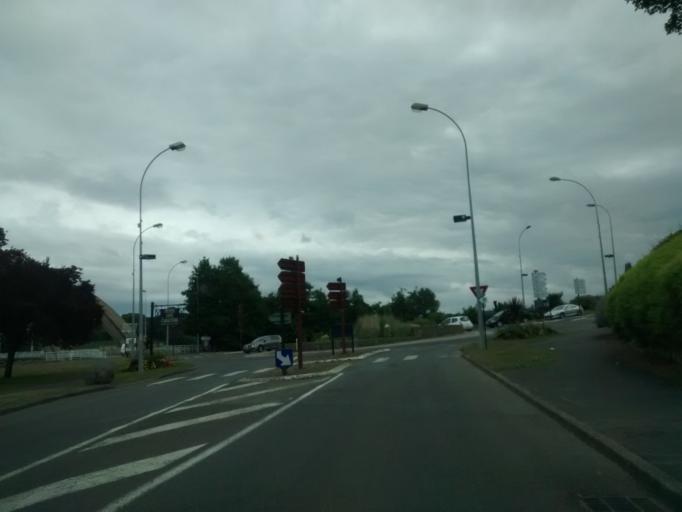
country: FR
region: Brittany
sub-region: Departement des Cotes-d'Armor
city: Minihy-Treguier
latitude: 48.7852
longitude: -3.2226
